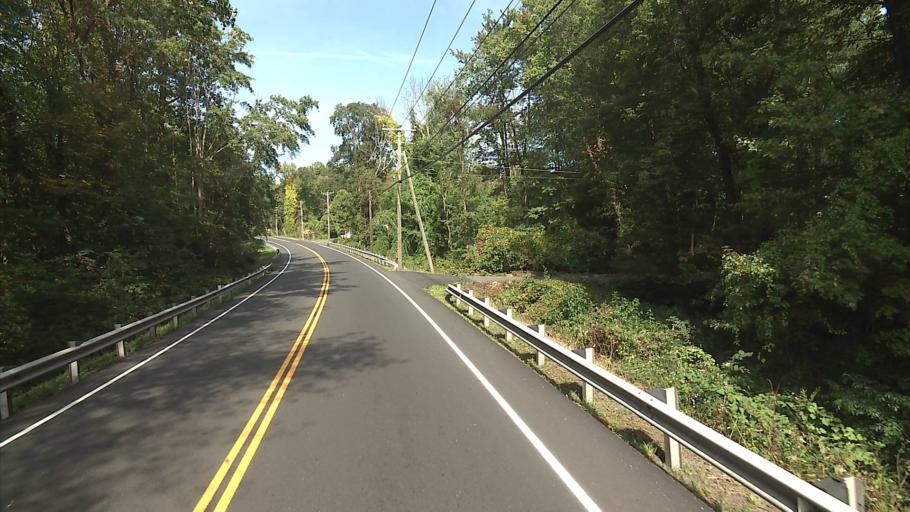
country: US
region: Connecticut
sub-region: New Haven County
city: Southbury
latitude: 41.3892
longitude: -73.2082
